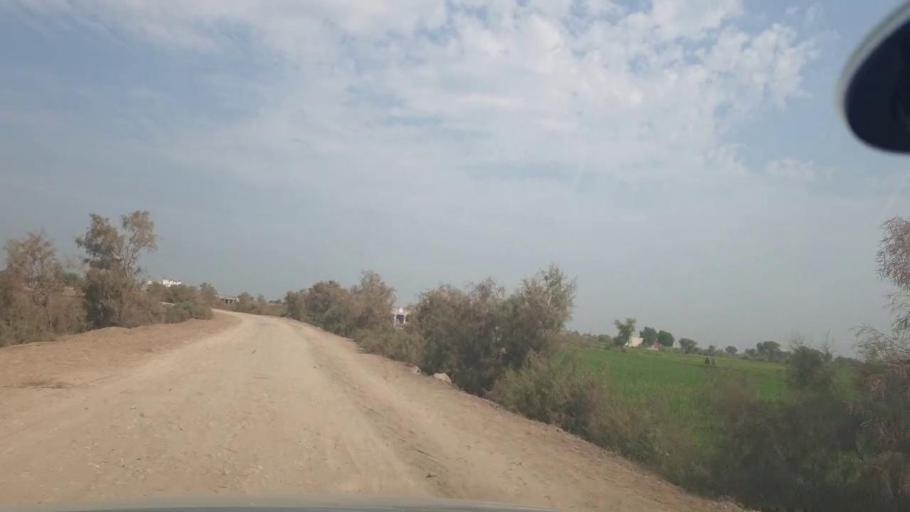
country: PK
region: Balochistan
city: Mehrabpur
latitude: 28.1268
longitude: 68.0890
